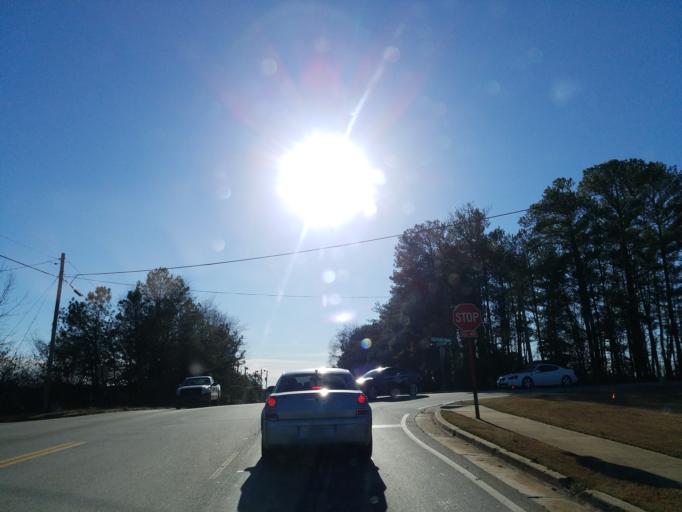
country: US
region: Georgia
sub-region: Cobb County
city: Mableton
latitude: 33.7797
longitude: -84.5371
